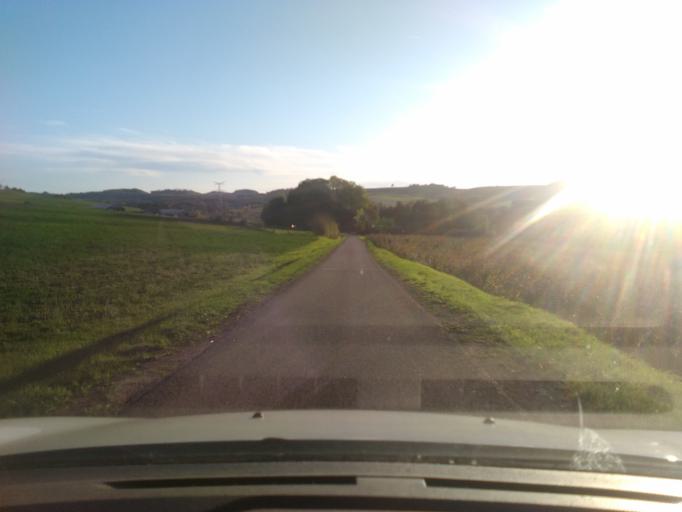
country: FR
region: Lorraine
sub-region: Departement des Vosges
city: Charmes
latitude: 48.3378
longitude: 6.2892
